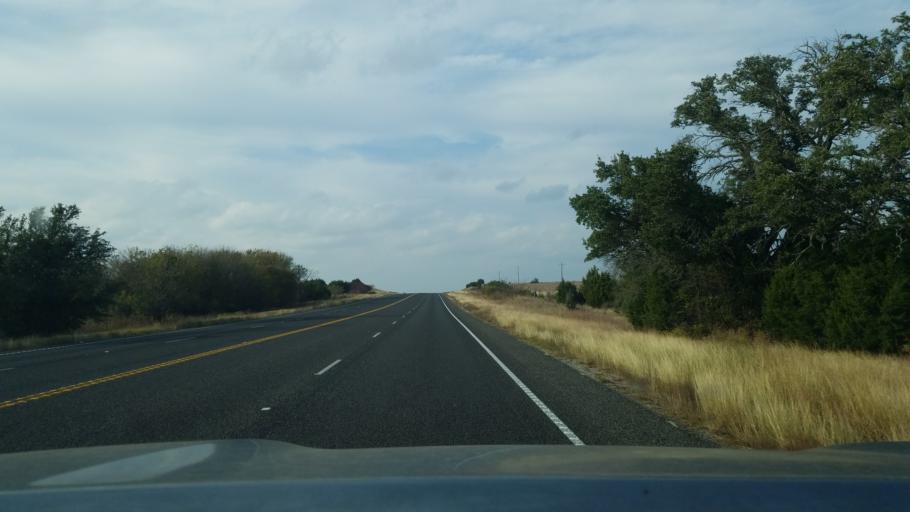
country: US
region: Texas
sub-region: Mills County
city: Goldthwaite
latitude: 31.3268
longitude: -98.4921
